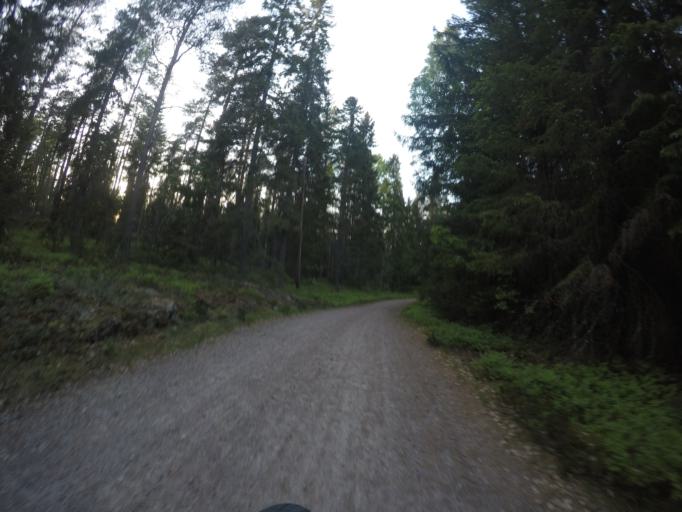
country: SE
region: Soedermanland
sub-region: Eskilstuna Kommun
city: Eskilstuna
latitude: 59.3396
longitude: 16.5107
